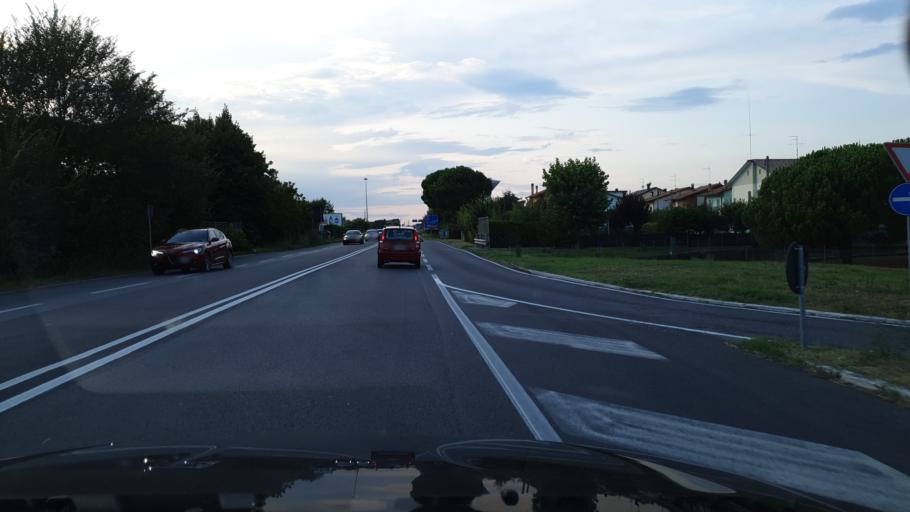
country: IT
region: Emilia-Romagna
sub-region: Forli-Cesena
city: Cesenatico
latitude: 44.1892
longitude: 12.4043
